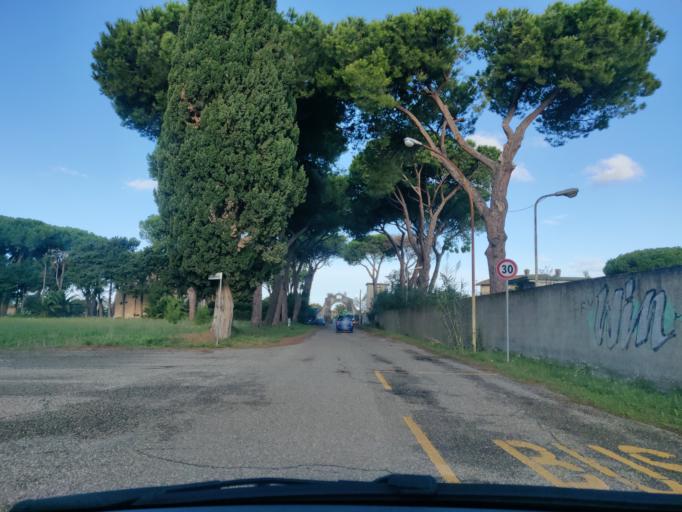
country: IT
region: Latium
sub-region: Citta metropolitana di Roma Capitale
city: Aurelia
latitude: 42.1385
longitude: 11.7848
